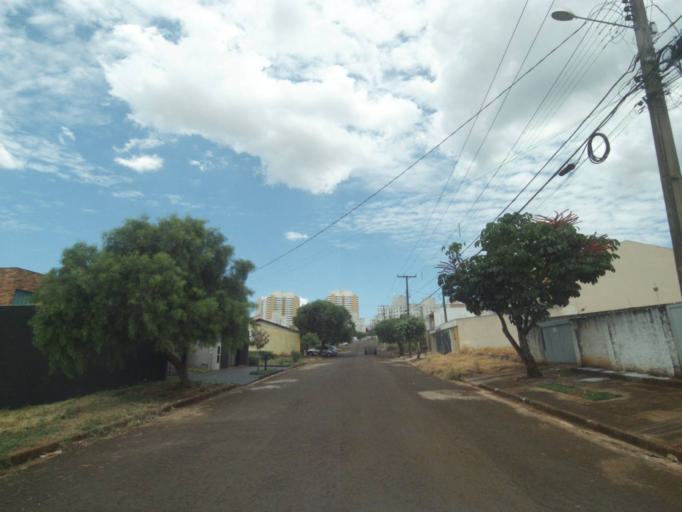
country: BR
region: Parana
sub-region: Londrina
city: Londrina
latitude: -23.3215
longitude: -51.1965
